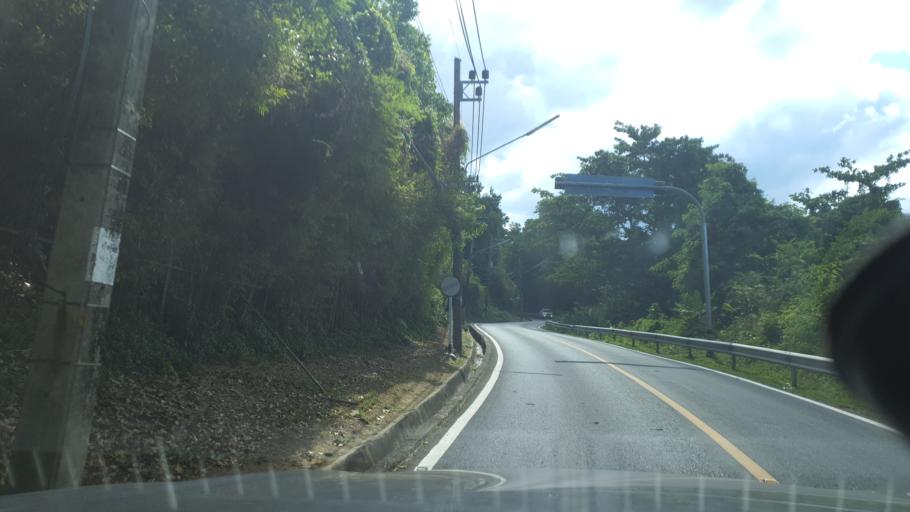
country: TH
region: Phuket
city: Thalang
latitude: 8.0532
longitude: 98.2782
